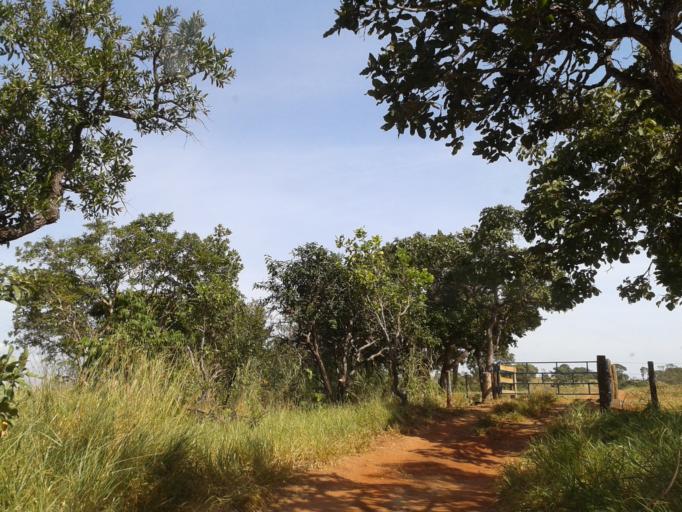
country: BR
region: Minas Gerais
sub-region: Campina Verde
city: Campina Verde
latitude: -19.5058
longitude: -49.5656
